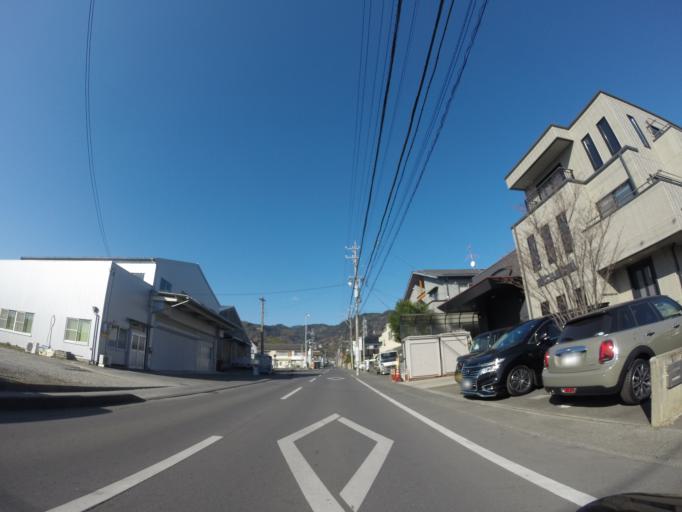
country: JP
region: Shizuoka
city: Shizuoka-shi
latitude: 35.0389
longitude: 138.4541
